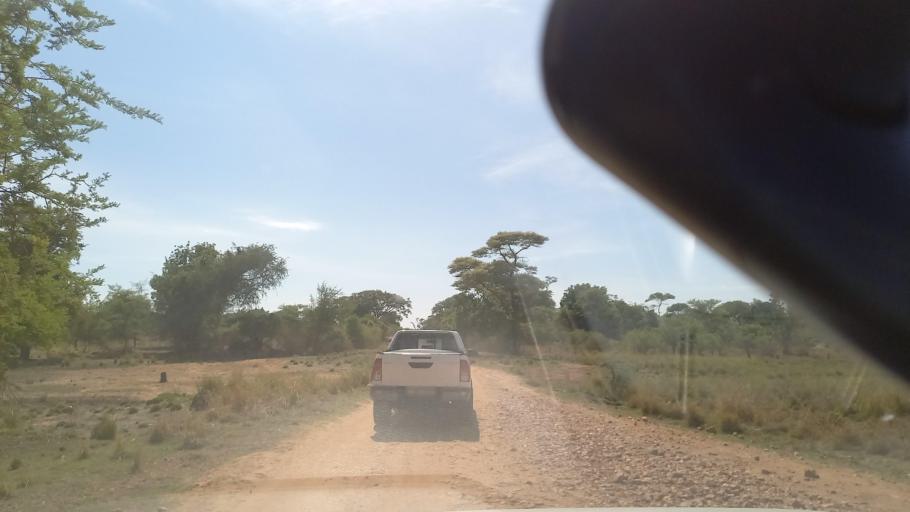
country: ZM
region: Southern
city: Mazabuka
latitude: -16.0404
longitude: 27.6197
